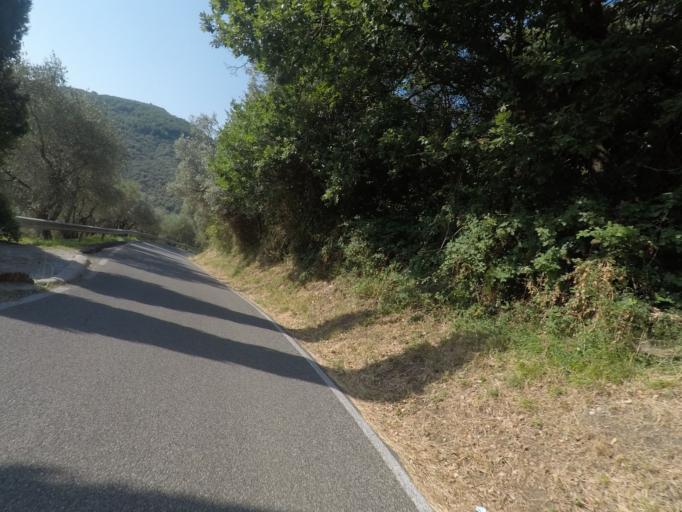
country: IT
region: Liguria
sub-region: Provincia di La Spezia
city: Casano-Dogana-Isola
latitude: 44.0893
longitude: 10.0495
